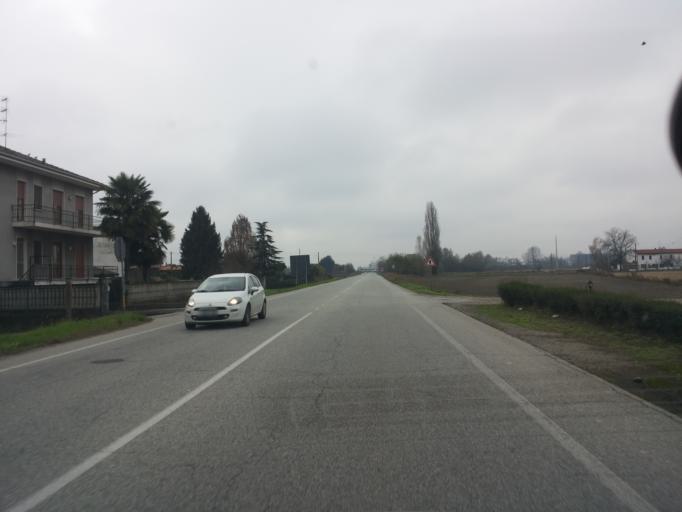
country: IT
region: Piedmont
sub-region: Provincia di Alessandria
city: Villanova Monferrato
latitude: 45.1791
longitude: 8.4723
